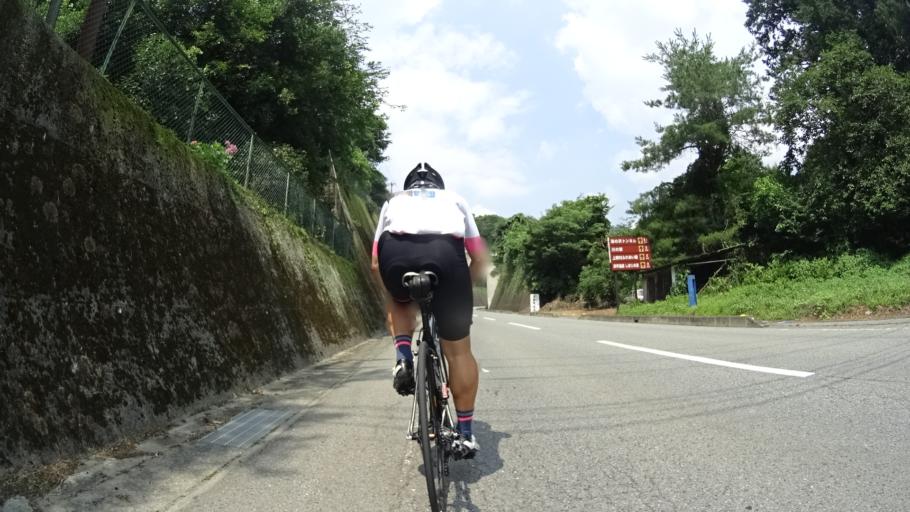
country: JP
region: Gunma
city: Tomioka
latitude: 36.0807
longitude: 138.7753
